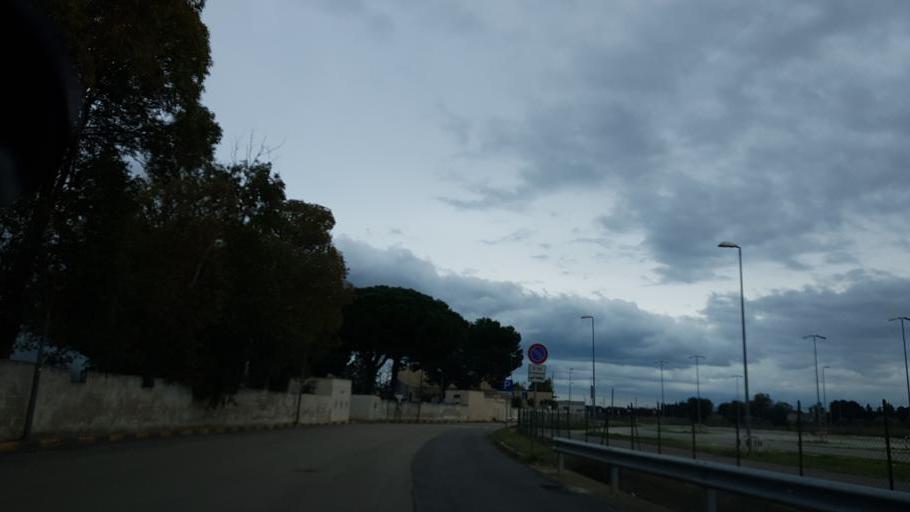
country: IT
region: Apulia
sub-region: Provincia di Brindisi
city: La Rosa
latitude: 40.6141
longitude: 17.9450
